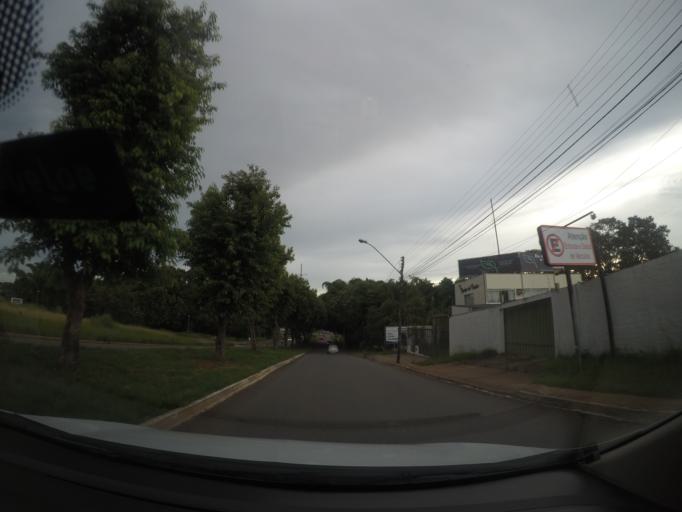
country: BR
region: Goias
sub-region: Goiania
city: Goiania
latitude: -16.7375
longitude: -49.3118
